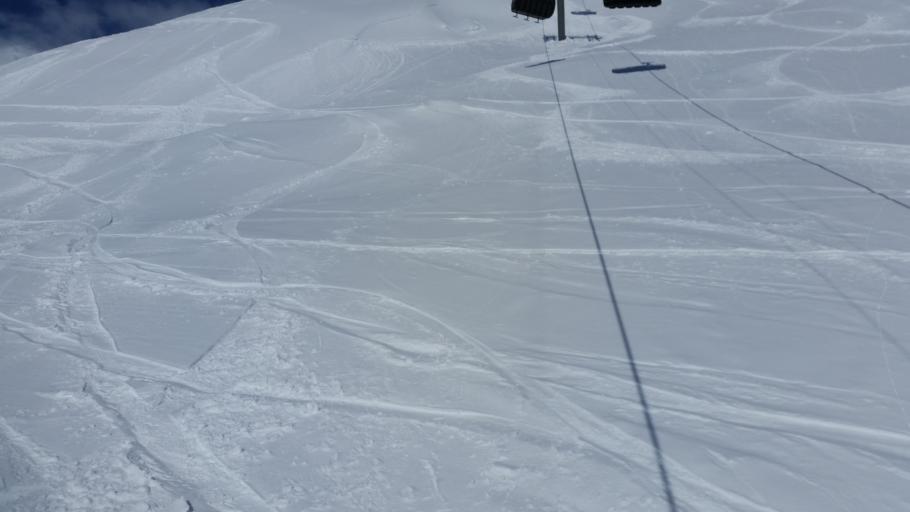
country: CH
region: Grisons
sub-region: Surselva District
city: Ilanz
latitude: 46.8521
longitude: 9.1628
